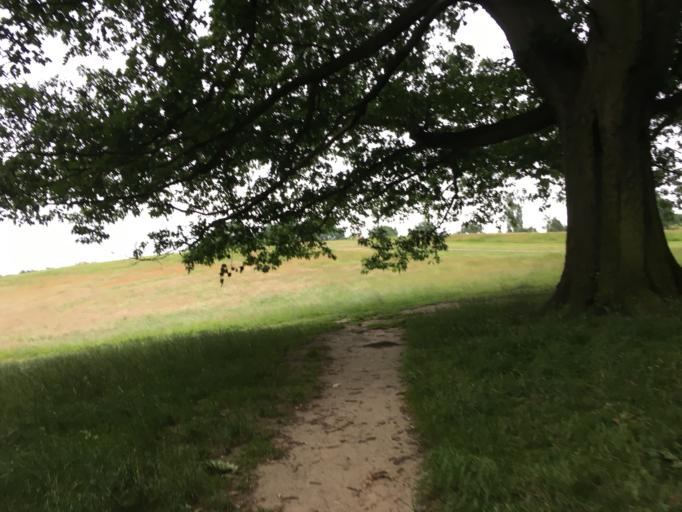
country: GB
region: England
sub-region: Greater London
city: Belsize Park
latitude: 51.5608
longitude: -0.1602
